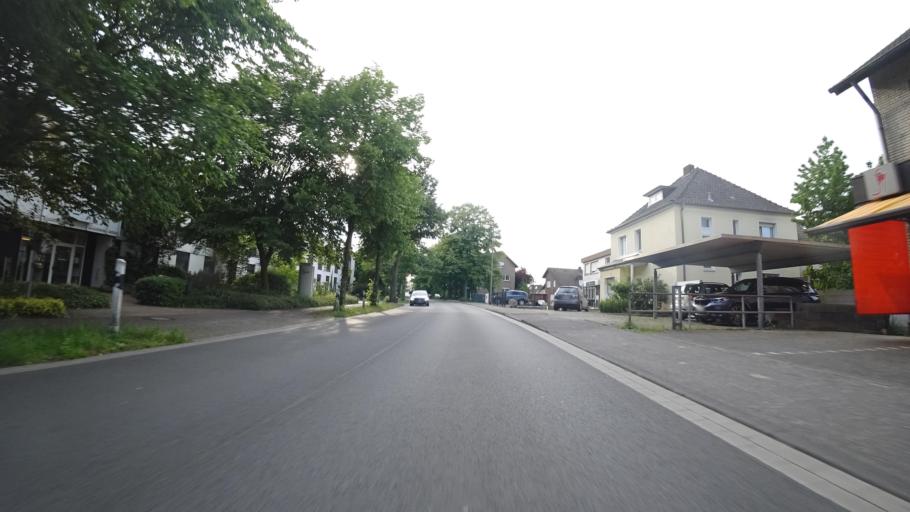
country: DE
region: North Rhine-Westphalia
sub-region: Regierungsbezirk Detmold
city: Guetersloh
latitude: 51.9118
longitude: 8.4192
